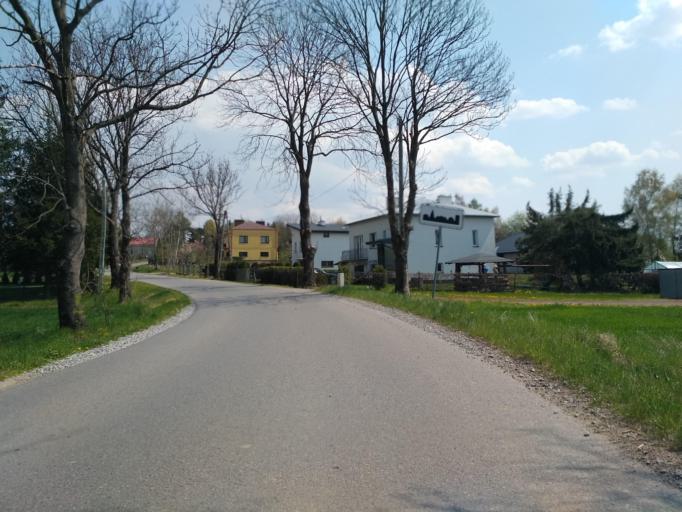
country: PL
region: Subcarpathian Voivodeship
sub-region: Powiat jasielski
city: Tarnowiec
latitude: 49.7450
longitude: 21.5605
